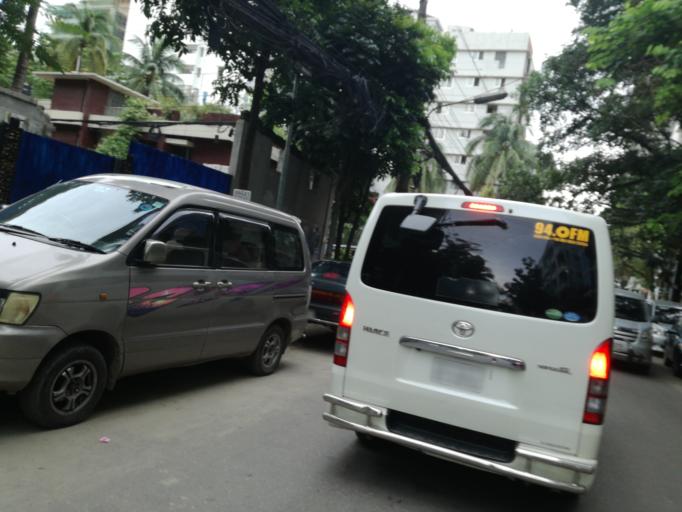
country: BD
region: Dhaka
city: Paltan
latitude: 23.7822
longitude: 90.4153
